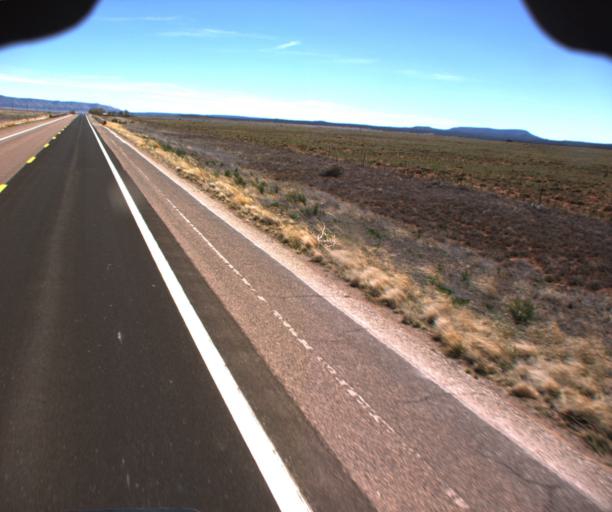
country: US
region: Arizona
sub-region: Mohave County
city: Peach Springs
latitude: 35.4843
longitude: -113.1471
